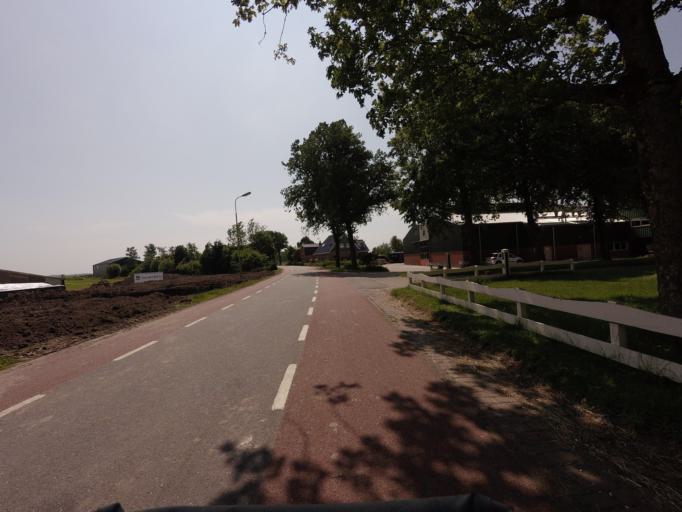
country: NL
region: North Holland
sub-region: Gemeente Opmeer
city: Opmeer
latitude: 52.6869
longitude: 4.9434
